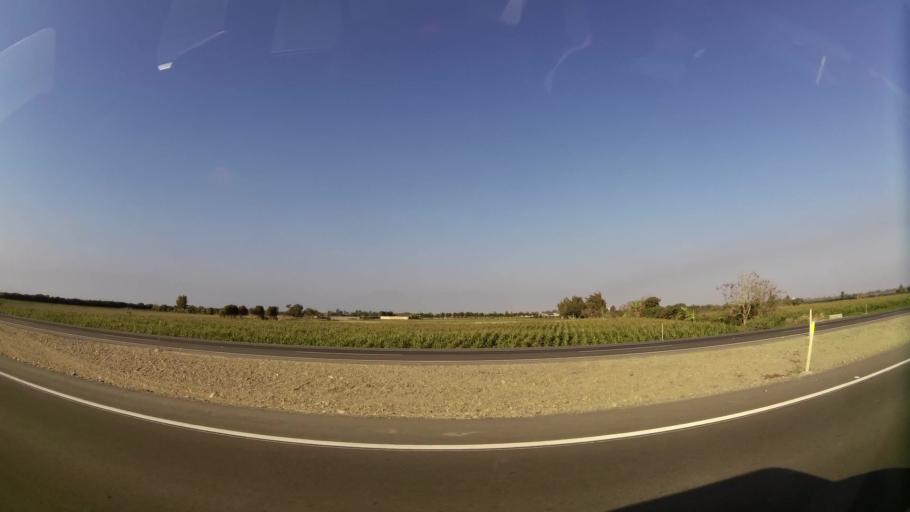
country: PE
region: Ica
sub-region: Provincia de Chincha
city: Chincha Baja
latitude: -13.5159
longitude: -76.1839
